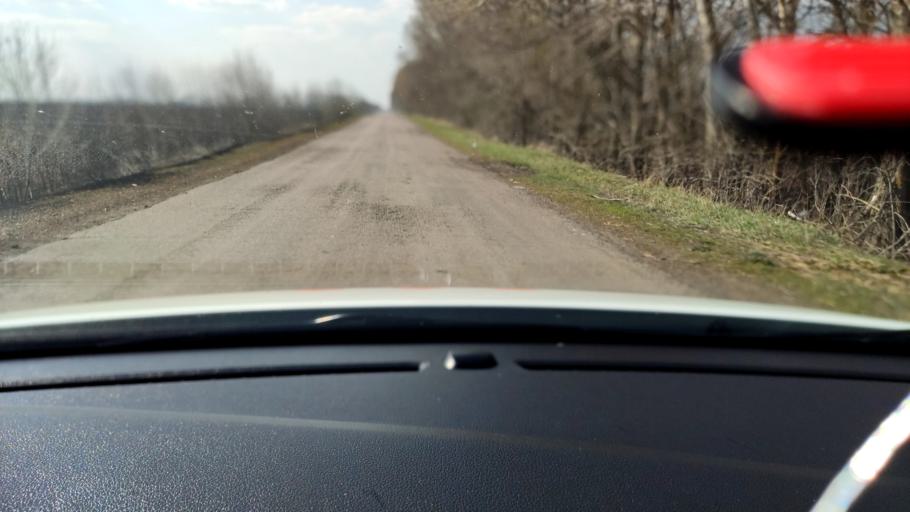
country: RU
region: Voronezj
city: Uryv-Pokrovka
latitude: 51.1269
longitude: 39.1126
